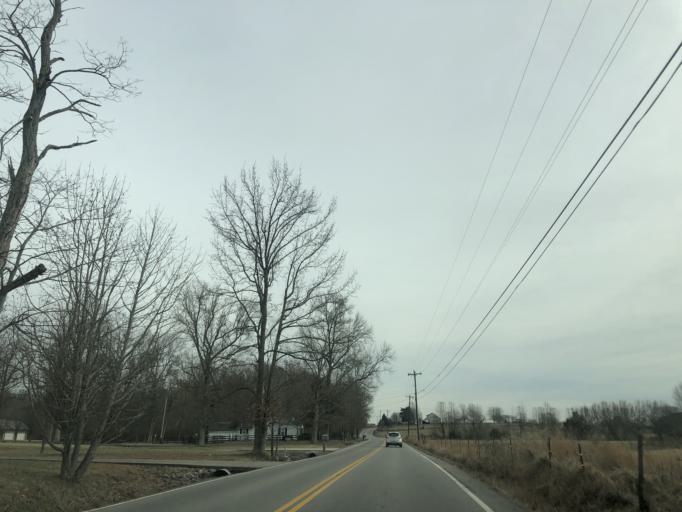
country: US
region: Tennessee
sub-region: Sumner County
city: White House
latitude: 36.4870
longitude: -86.5832
